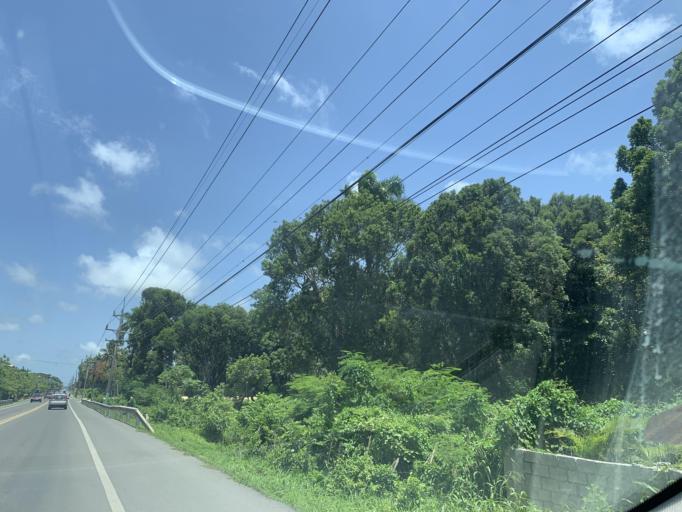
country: DO
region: Puerto Plata
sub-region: Puerto Plata
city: Puerto Plata
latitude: 19.7503
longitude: -70.5757
